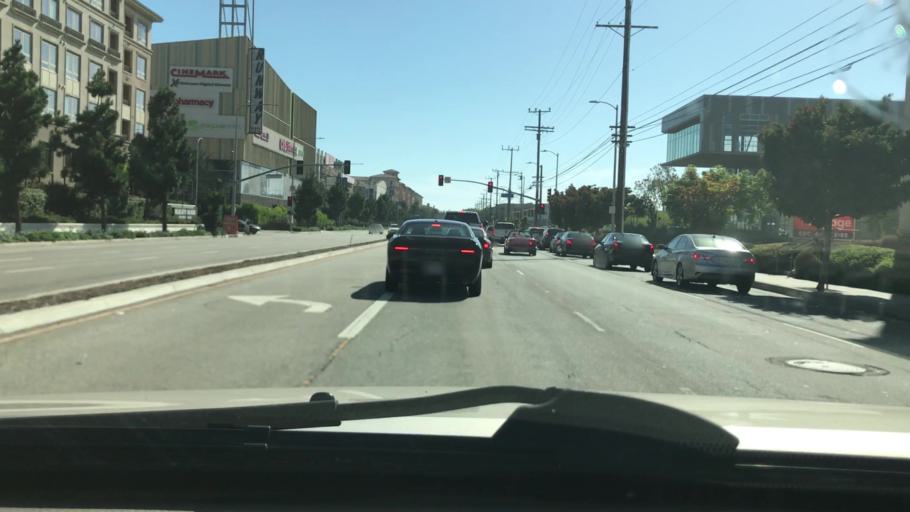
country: US
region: California
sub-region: Los Angeles County
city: Marina del Rey
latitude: 33.9786
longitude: -118.4155
